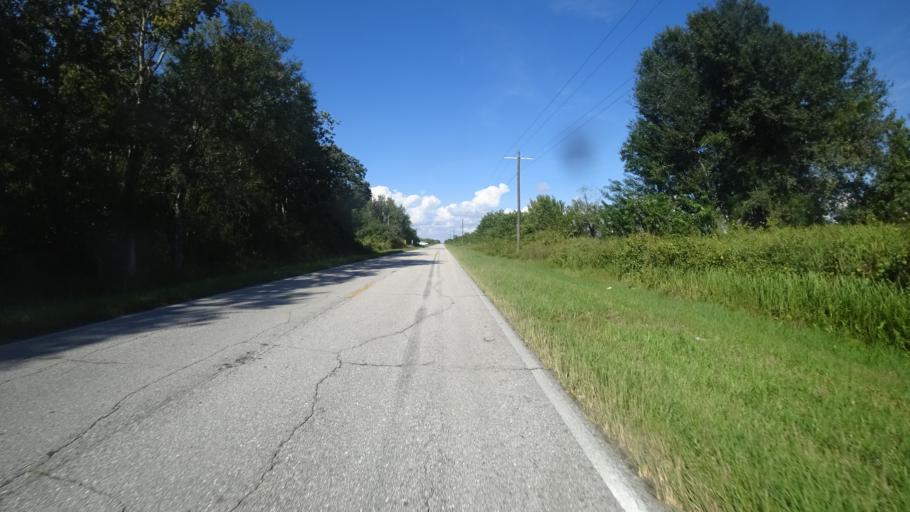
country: US
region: Florida
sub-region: Sarasota County
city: The Meadows
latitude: 27.4369
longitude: -82.2707
